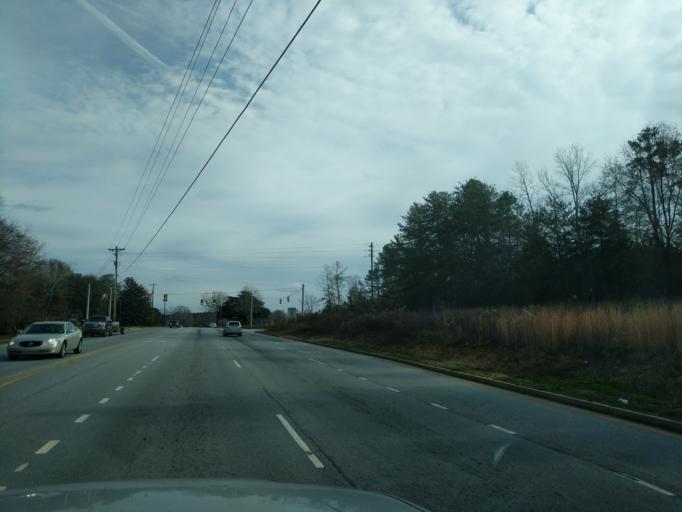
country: US
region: South Carolina
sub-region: Oconee County
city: Seneca
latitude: 34.7190
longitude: -83.0097
